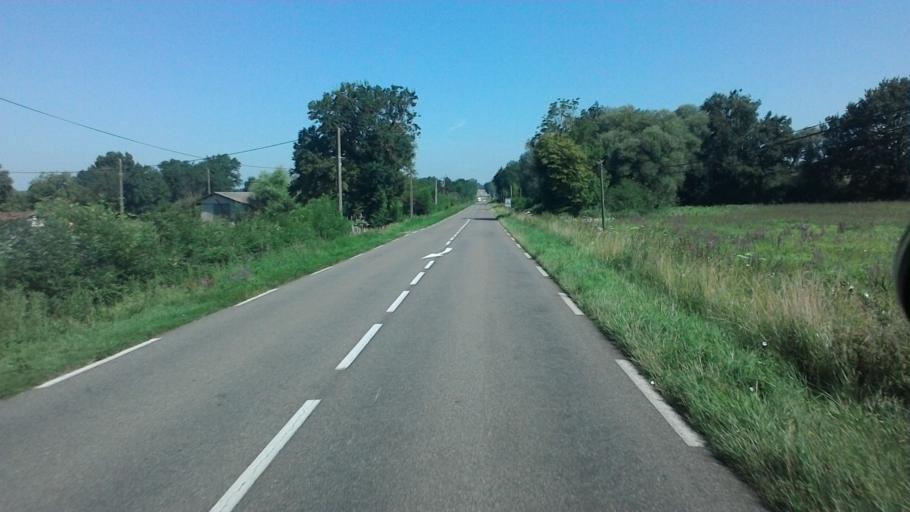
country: FR
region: Rhone-Alpes
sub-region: Departement de l'Ain
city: Saint-Trivier-de-Courtes
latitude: 46.4145
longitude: 5.1035
